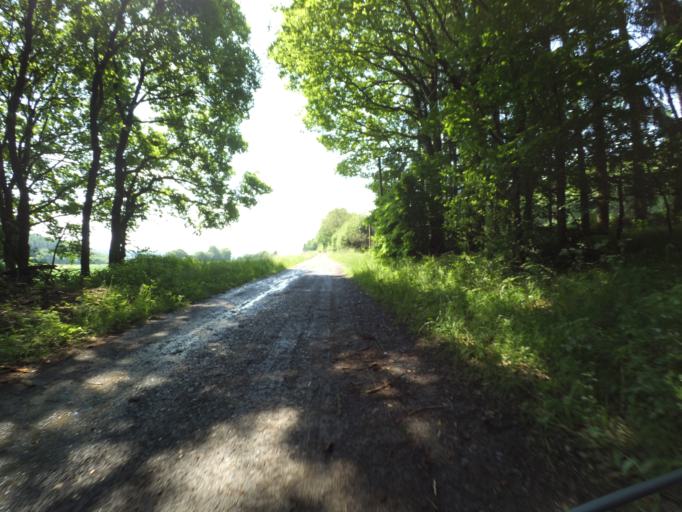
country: DE
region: Rheinland-Pfalz
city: Kalenborn
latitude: 50.2730
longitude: 7.0949
